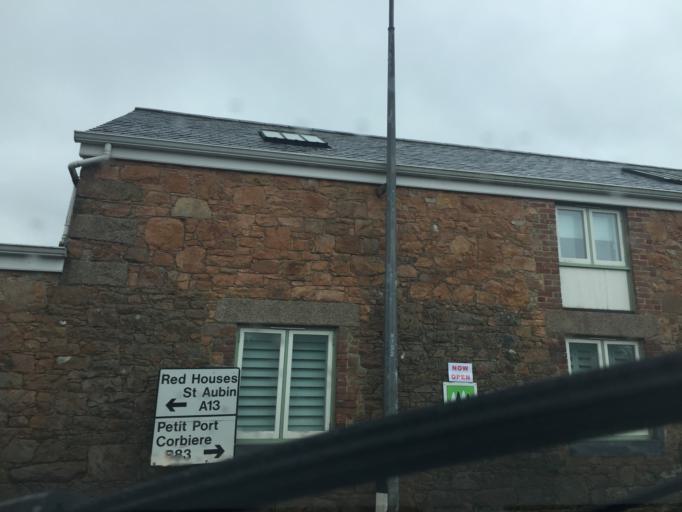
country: JE
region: St Helier
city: Saint Helier
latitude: 49.1853
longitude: -2.2181
